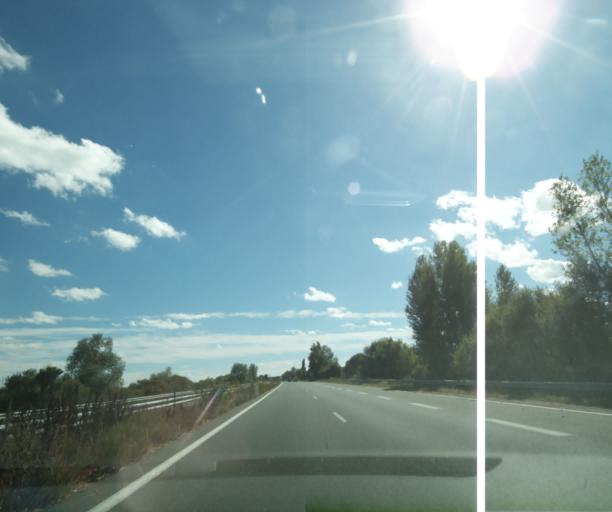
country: FR
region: Aquitaine
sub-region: Departement du Lot-et-Garonne
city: Damazan
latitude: 44.3391
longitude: 0.2526
